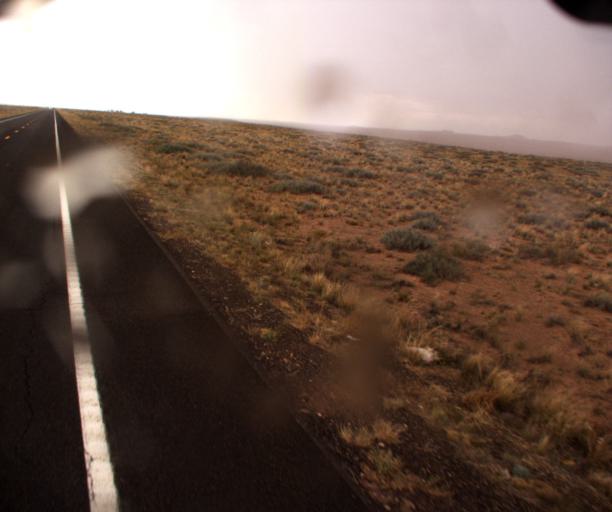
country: US
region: Arizona
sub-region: Coconino County
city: Tuba City
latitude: 36.1600
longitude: -111.1081
